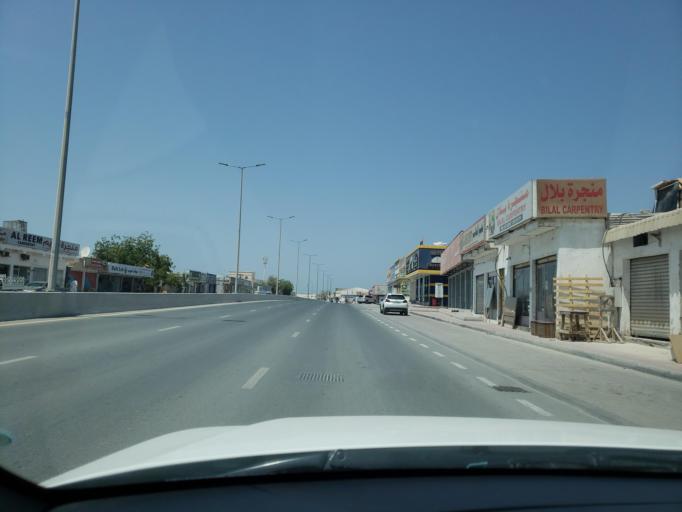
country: AE
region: Ra's al Khaymah
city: Ras al-Khaimah
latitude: 25.8157
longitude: 55.9730
